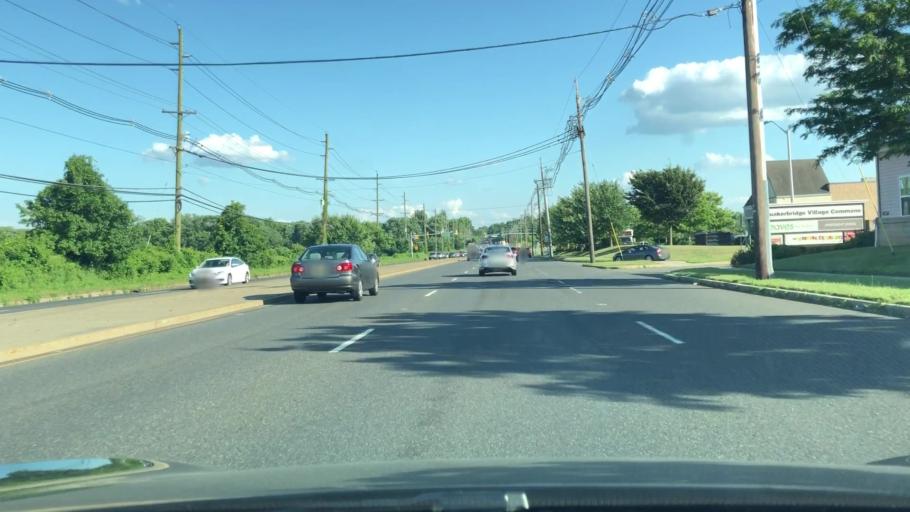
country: US
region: New Jersey
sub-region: Mercer County
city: Mercerville
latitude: 40.2861
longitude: -74.6746
